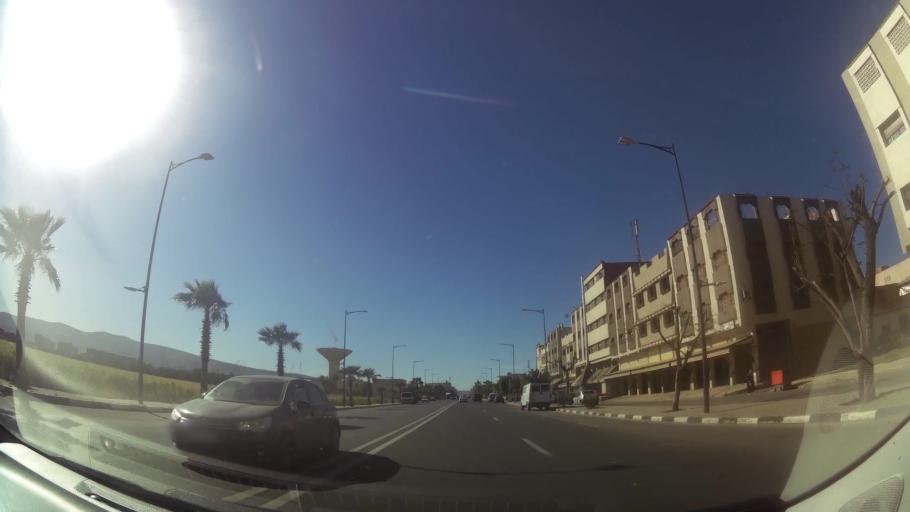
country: MA
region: Oriental
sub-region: Berkane-Taourirt
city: Ahfir
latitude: 34.8558
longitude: -1.9915
